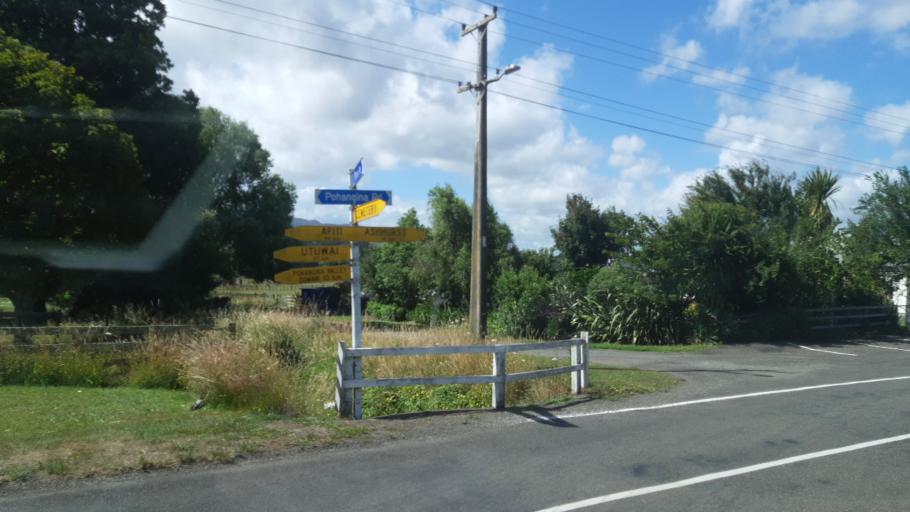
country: NZ
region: Manawatu-Wanganui
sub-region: Palmerston North City
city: Palmerston North
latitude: -40.1735
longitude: 175.7948
